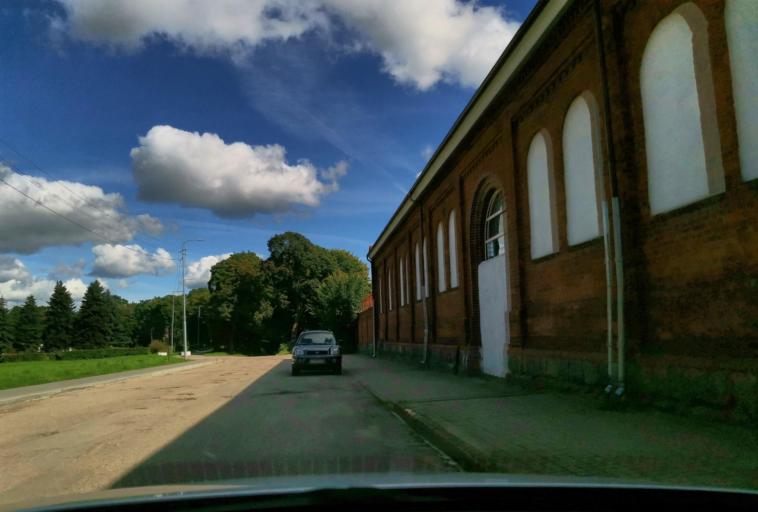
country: RU
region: Kaliningrad
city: Chernyakhovsk
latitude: 54.6368
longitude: 21.8190
